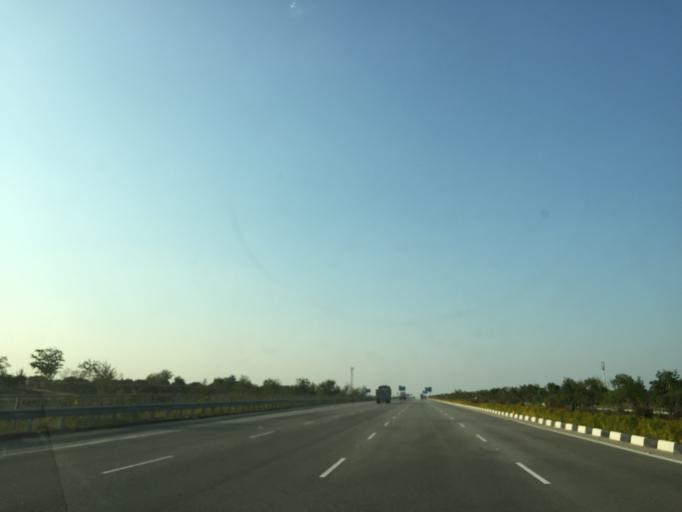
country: IN
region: Telangana
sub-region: Rangareddi
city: Ghatkesar
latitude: 17.5063
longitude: 78.6539
